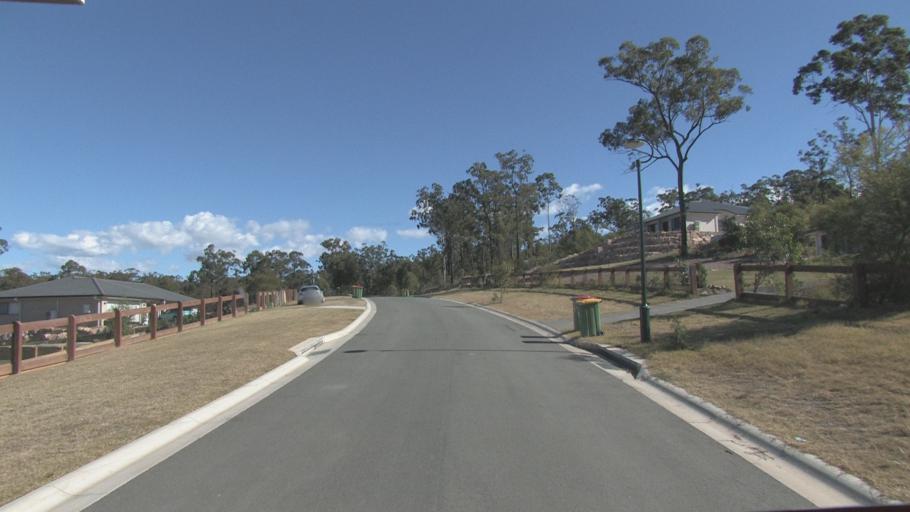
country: AU
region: Queensland
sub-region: Ipswich
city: Springfield Lakes
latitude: -27.7333
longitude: 152.9048
